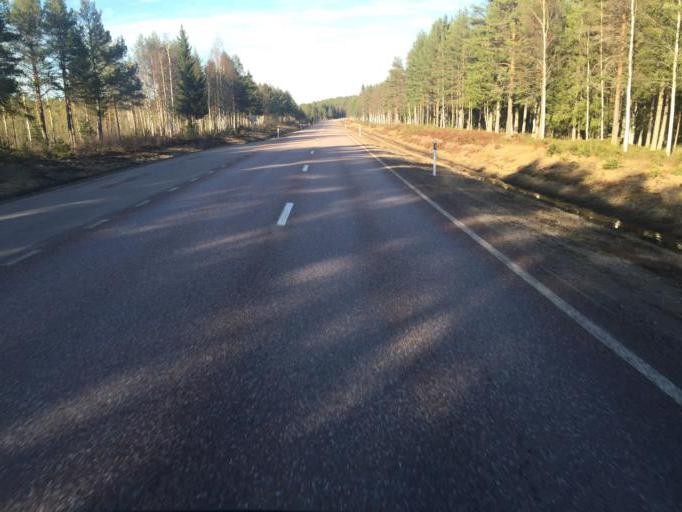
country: SE
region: Dalarna
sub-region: Vansbro Kommun
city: Jarna
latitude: 60.4671
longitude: 14.6021
